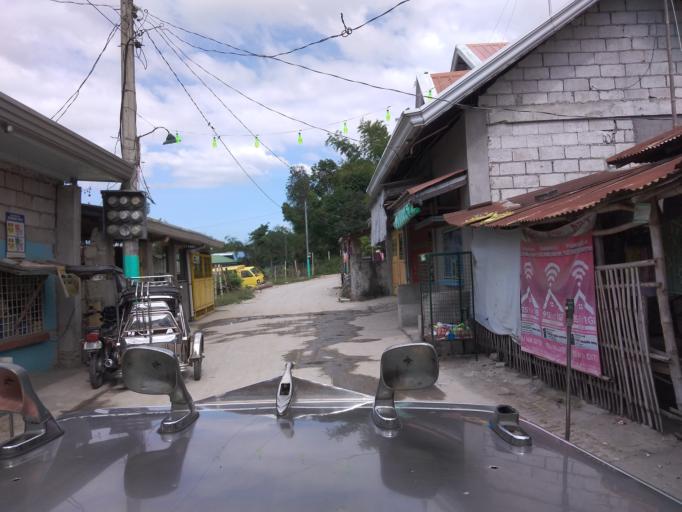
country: PH
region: Central Luzon
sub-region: Province of Pampanga
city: San Patricio
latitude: 15.1116
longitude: 120.7188
